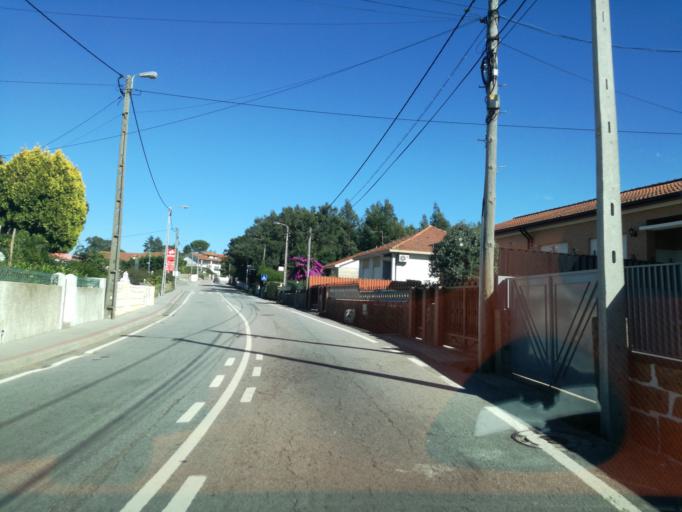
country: PT
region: Porto
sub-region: Trofa
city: Sao Romao do Coronado
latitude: 41.2751
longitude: -8.5438
